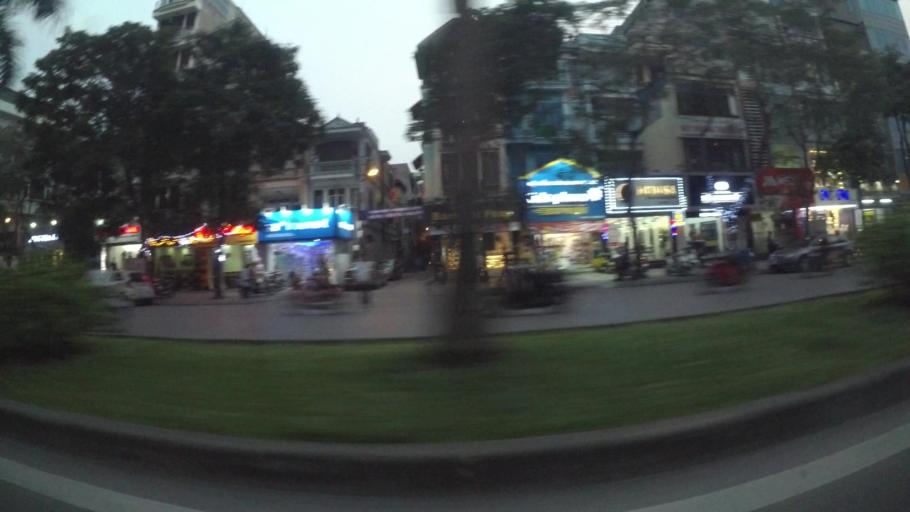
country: VN
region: Ha Noi
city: Ha Dong
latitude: 20.9770
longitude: 105.7884
